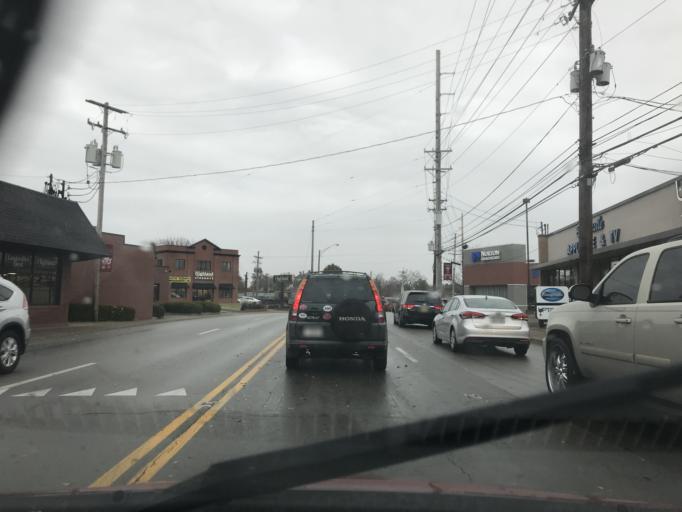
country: US
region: Kentucky
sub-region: Jefferson County
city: West Buechel
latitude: 38.2235
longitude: -85.6866
